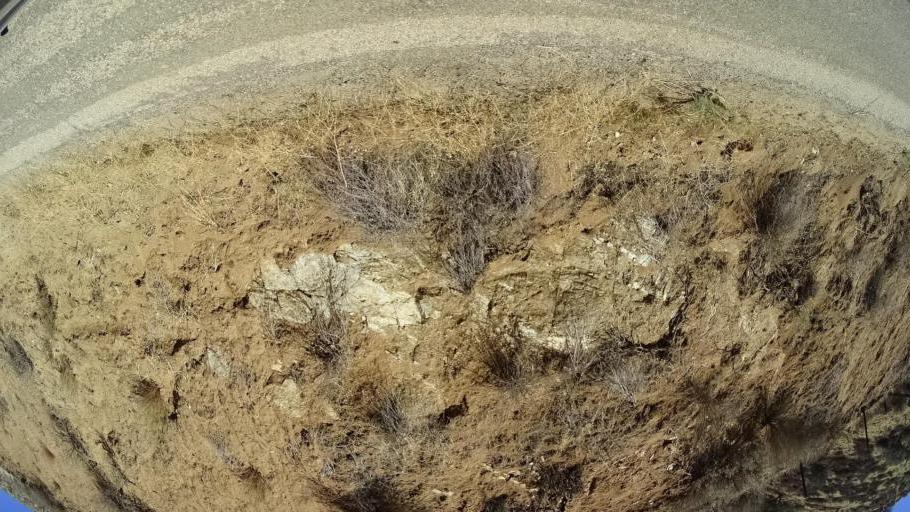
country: US
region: California
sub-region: Monterey County
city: King City
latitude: 36.2861
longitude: -120.9883
